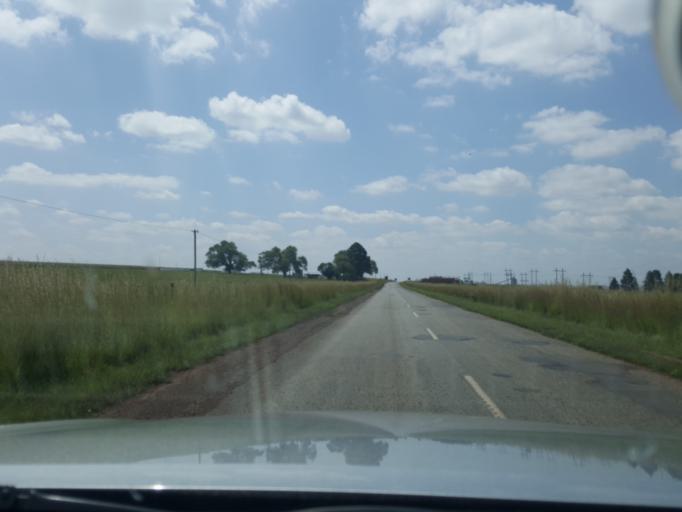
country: ZA
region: Mpumalanga
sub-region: Nkangala District Municipality
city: Middelburg
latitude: -26.0090
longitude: 29.4498
